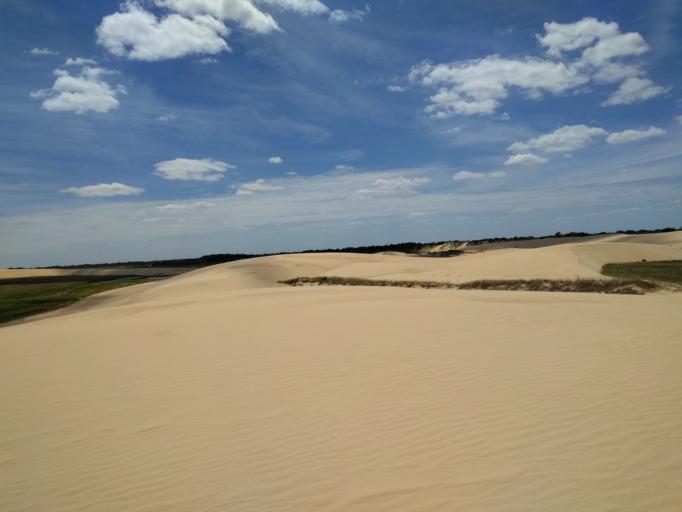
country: BO
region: Santa Cruz
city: Santa Cruz de la Sierra
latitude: -17.9479
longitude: -63.1519
